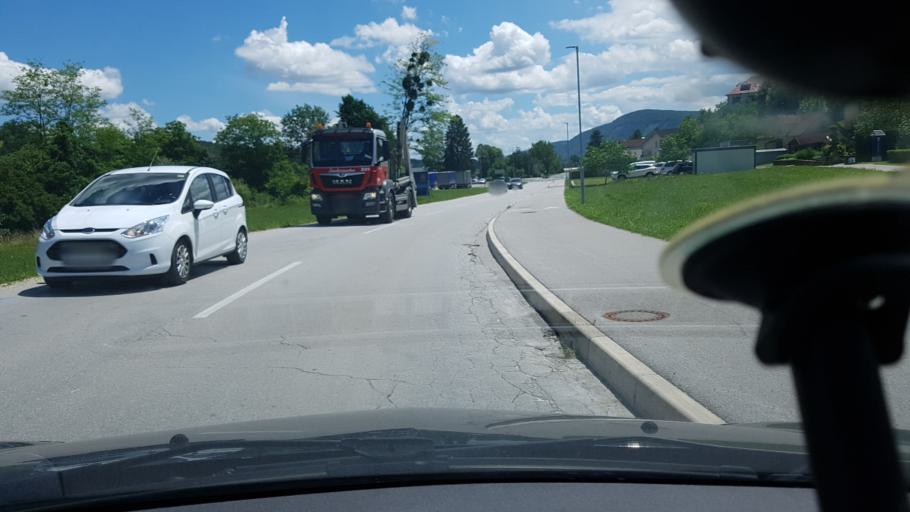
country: SI
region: Zrece
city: Zrece
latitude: 46.3717
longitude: 15.3916
